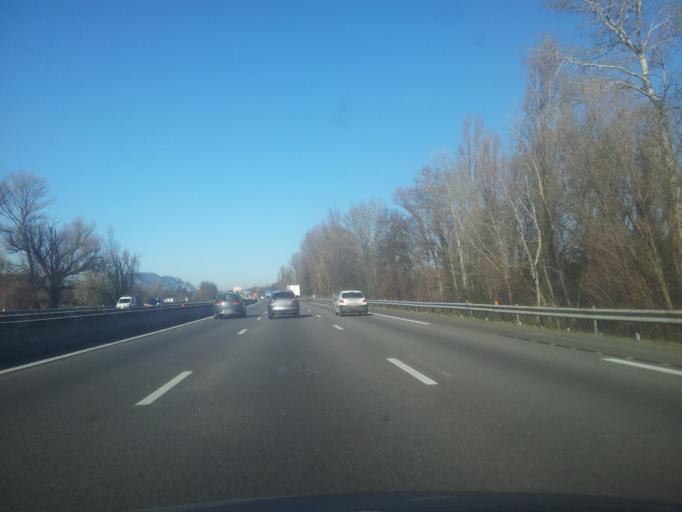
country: FR
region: Rhone-Alpes
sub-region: Departement de la Drome
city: Portes-les-Valence
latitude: 44.8569
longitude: 4.8668
